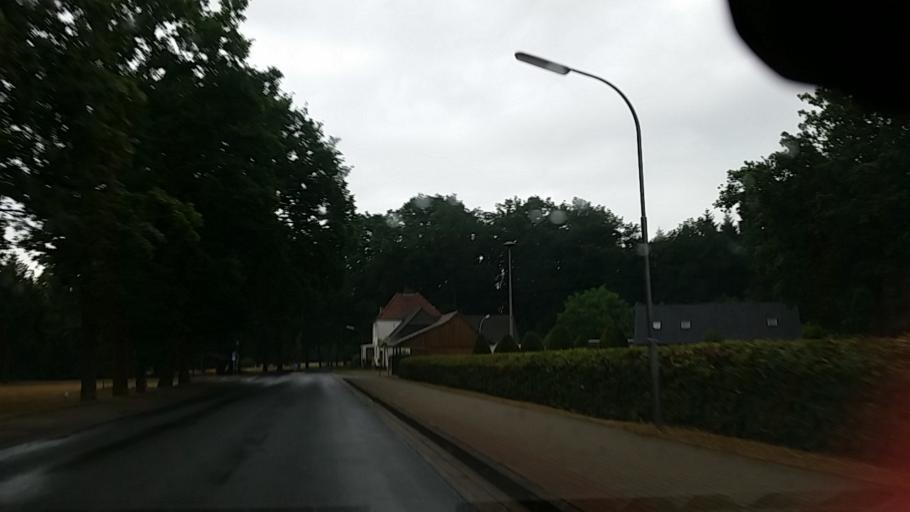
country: DE
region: Lower Saxony
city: Bokensdorf
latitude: 52.5011
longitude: 10.7161
